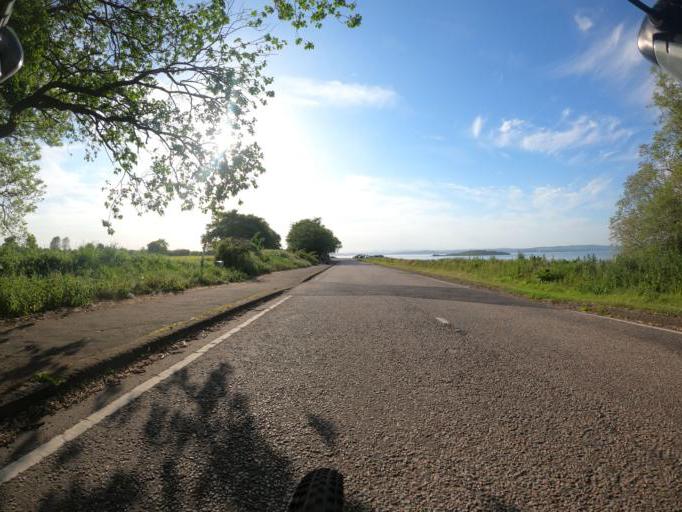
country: GB
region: Scotland
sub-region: Edinburgh
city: Colinton
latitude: 55.9786
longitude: -3.2724
